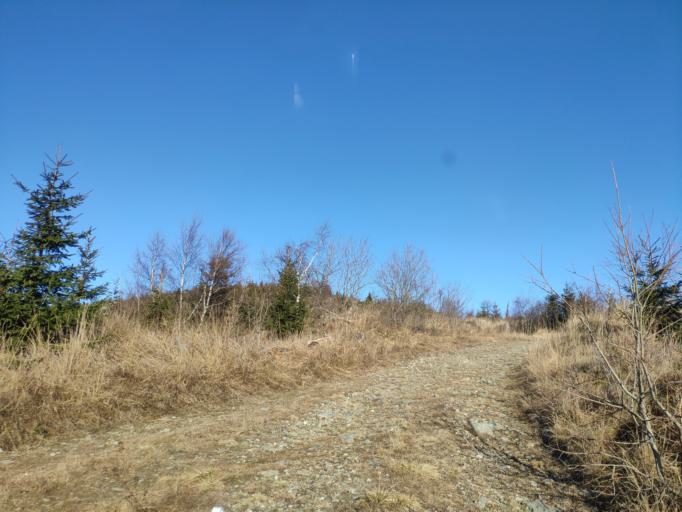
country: SK
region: Kosicky
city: Dobsina
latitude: 48.8261
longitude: 20.4634
